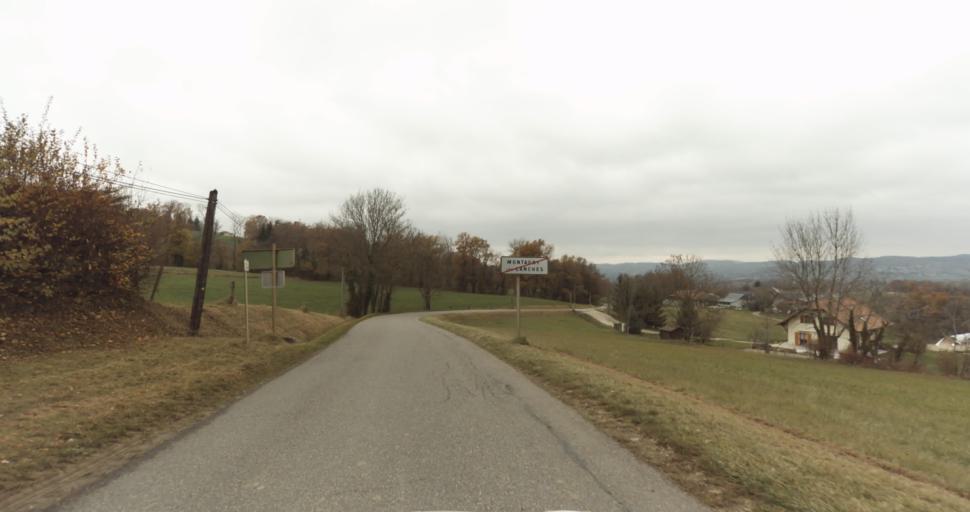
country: FR
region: Rhone-Alpes
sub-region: Departement de la Haute-Savoie
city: Chavanod
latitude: 45.8647
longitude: 6.0443
